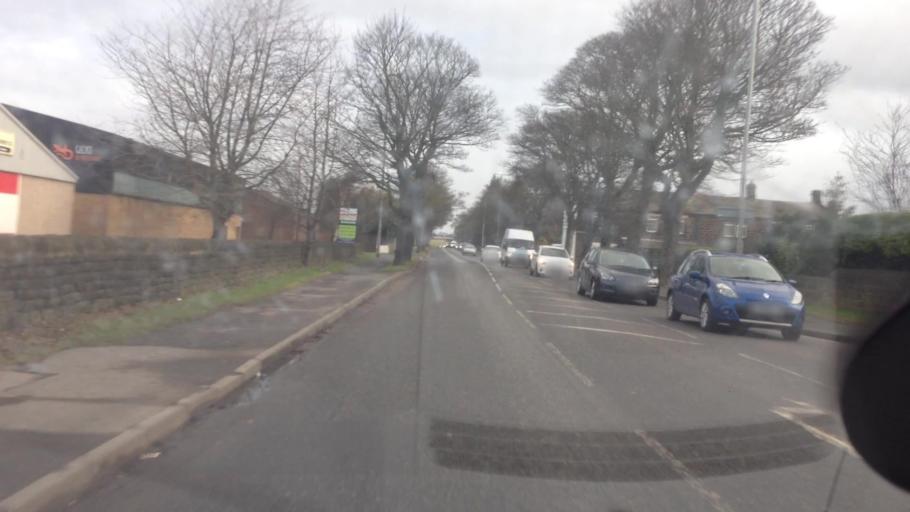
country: GB
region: England
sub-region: City and Borough of Leeds
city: Yeadon
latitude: 53.8641
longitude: -1.6719
